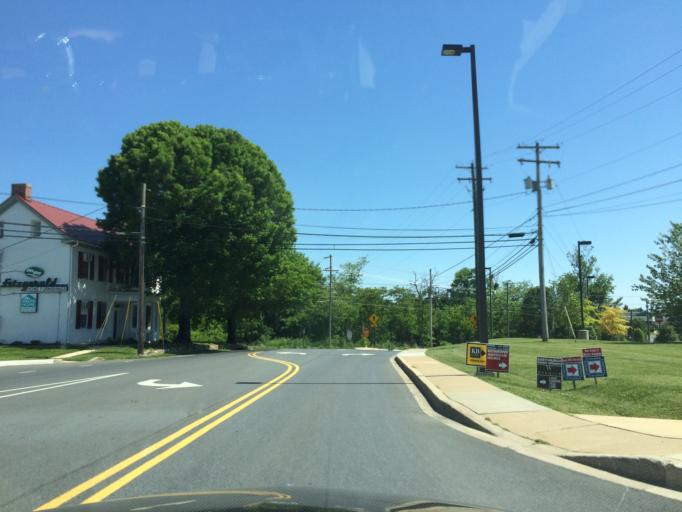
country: US
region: Maryland
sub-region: Frederick County
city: Frederick
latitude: 39.4444
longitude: -77.3952
